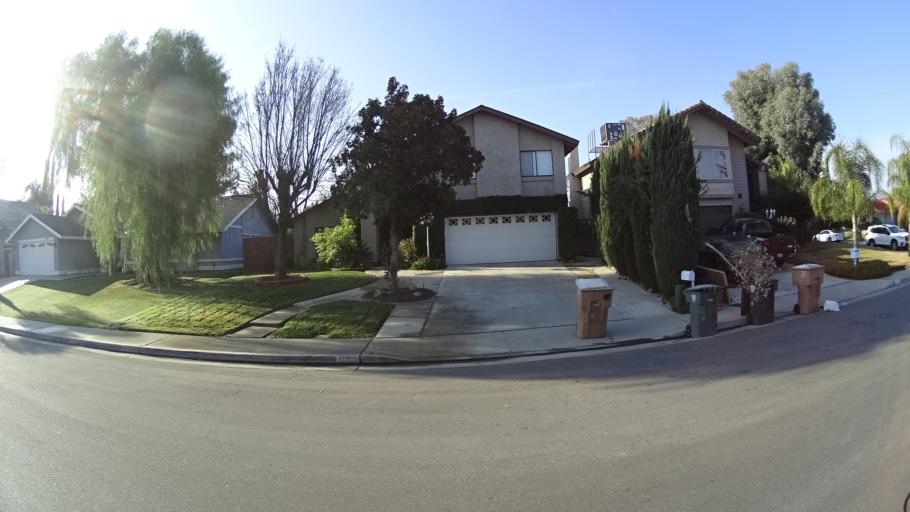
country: US
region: California
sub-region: Kern County
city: Oildale
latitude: 35.4044
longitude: -118.9353
